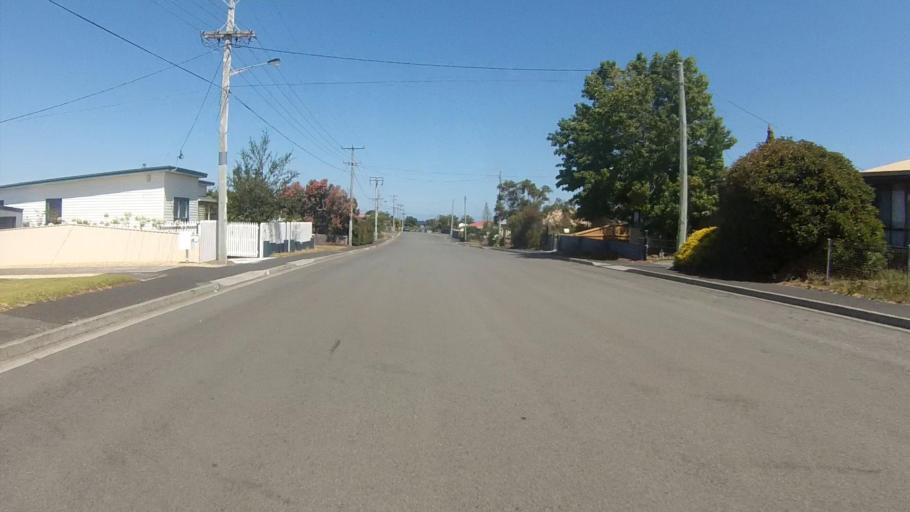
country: AU
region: Tasmania
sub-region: Sorell
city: Sorell
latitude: -42.8002
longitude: 147.5341
